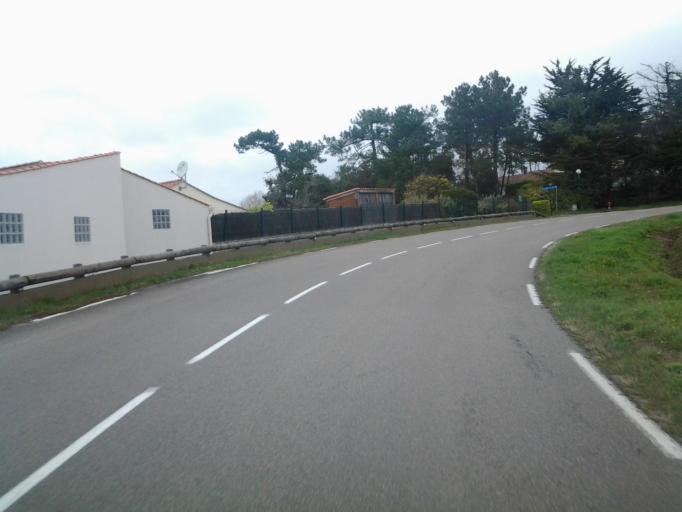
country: FR
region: Pays de la Loire
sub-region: Departement de la Vendee
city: Longeville-sur-Mer
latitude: 46.3944
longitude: -1.4850
